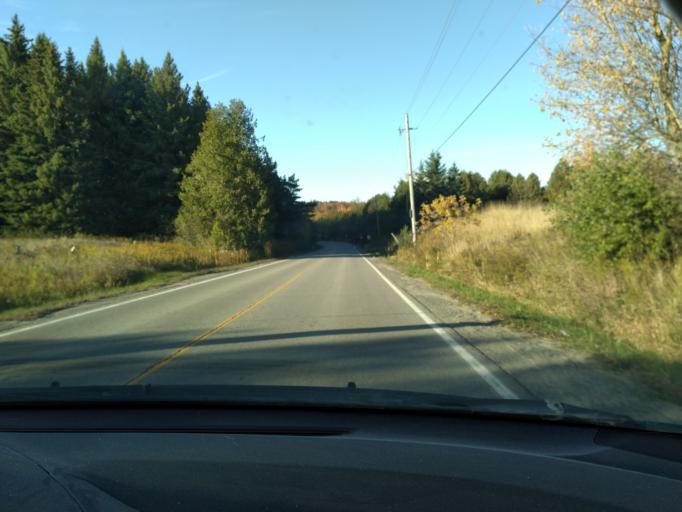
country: CA
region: Ontario
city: Vaughan
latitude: 43.9008
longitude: -79.7032
